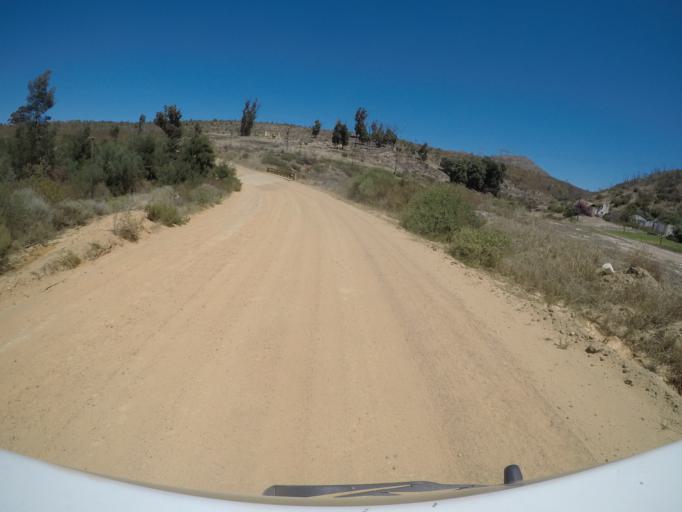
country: ZA
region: Western Cape
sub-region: Overberg District Municipality
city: Grabouw
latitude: -34.2178
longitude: 19.2046
